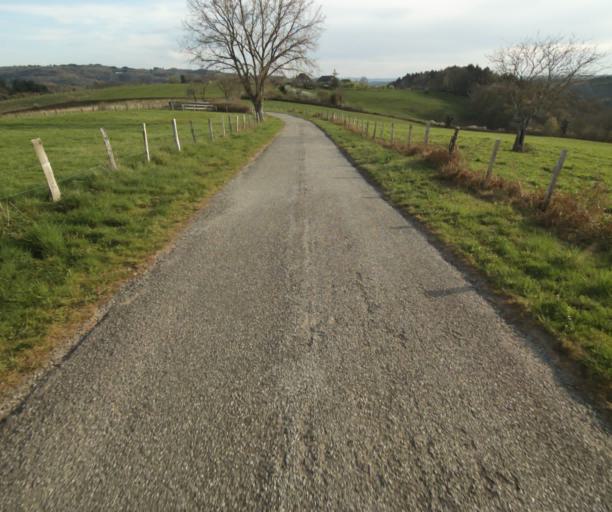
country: FR
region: Limousin
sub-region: Departement de la Correze
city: Correze
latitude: 45.3687
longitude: 1.8327
